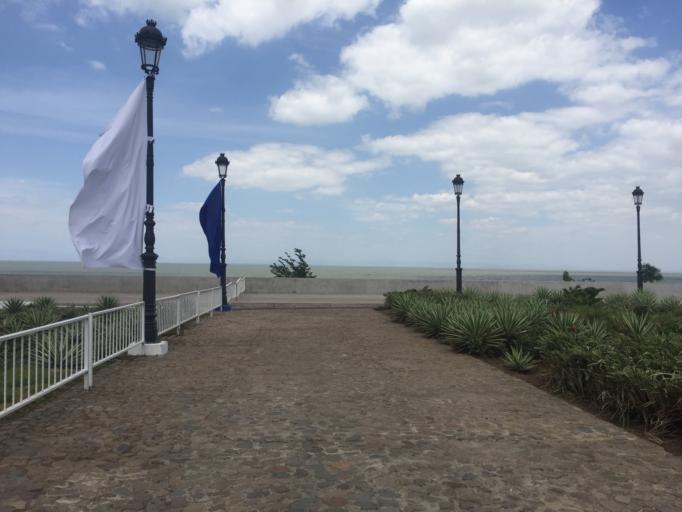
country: NI
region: Managua
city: Managua
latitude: 12.1601
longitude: -86.2725
